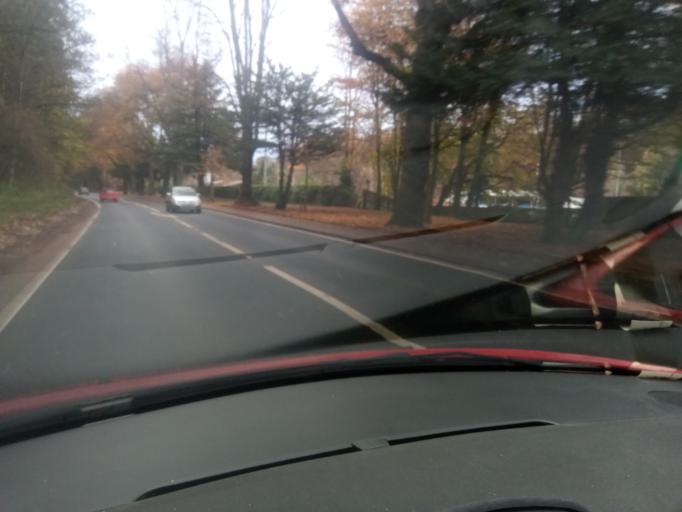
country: GB
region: Scotland
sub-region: The Scottish Borders
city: Jedburgh
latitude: 55.4913
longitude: -2.5450
